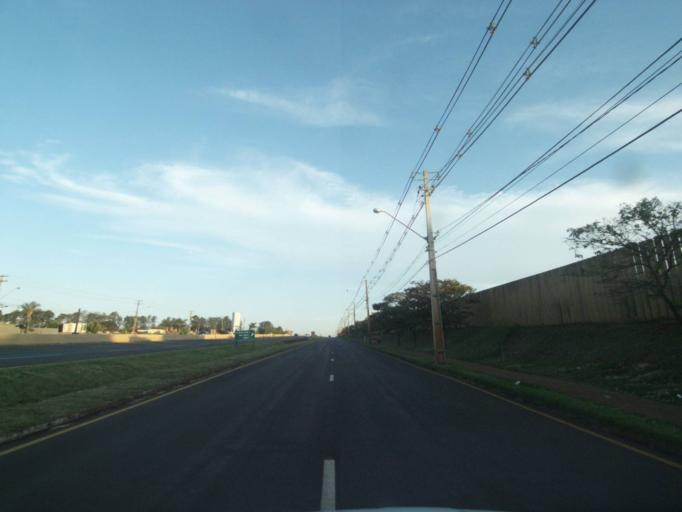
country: BR
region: Parana
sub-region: Londrina
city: Londrina
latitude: -23.3557
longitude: -51.1596
